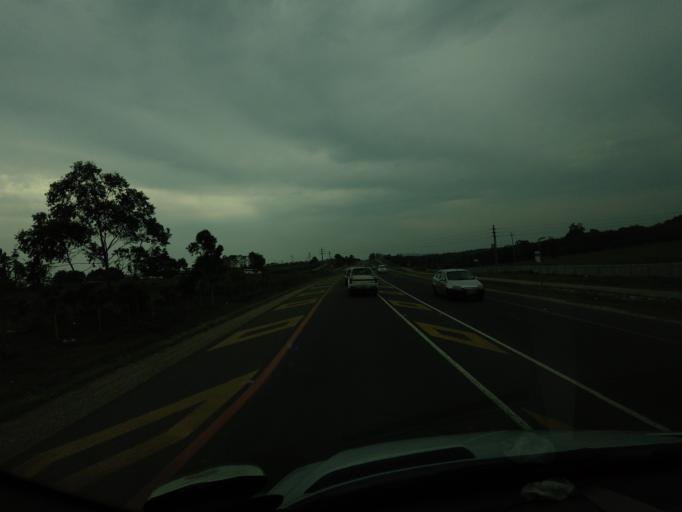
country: ZA
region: Western Cape
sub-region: Eden District Municipality
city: Plettenberg Bay
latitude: -34.0480
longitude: 23.3306
